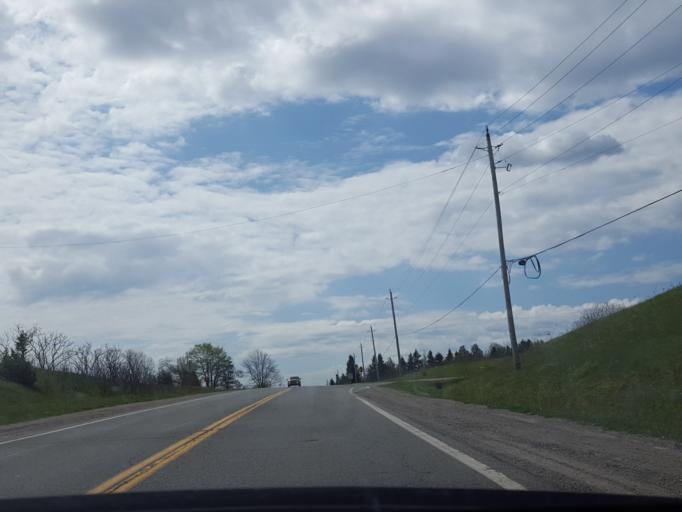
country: CA
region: Ontario
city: Oshawa
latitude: 43.9256
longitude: -78.7083
